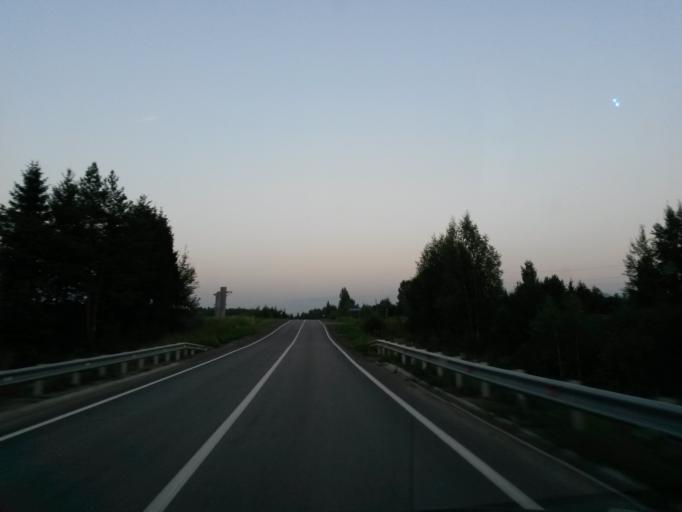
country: RU
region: Jaroslavl
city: Konstantinovskiy
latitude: 57.8112
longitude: 39.7306
